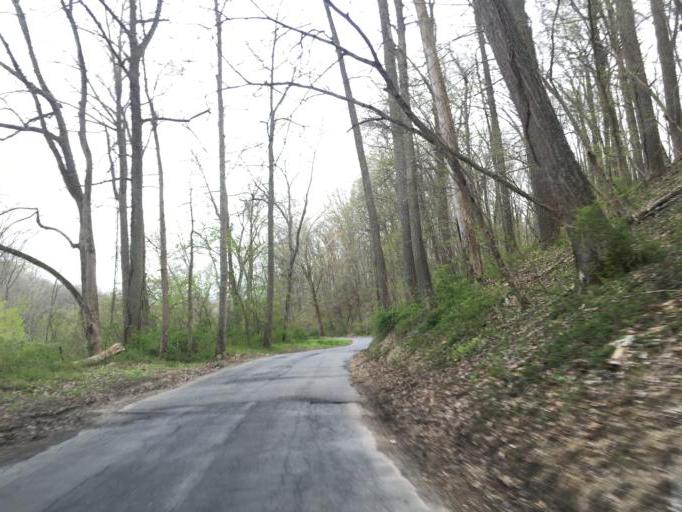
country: US
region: Maryland
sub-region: Baltimore County
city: Hunt Valley
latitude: 39.5557
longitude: -76.6400
